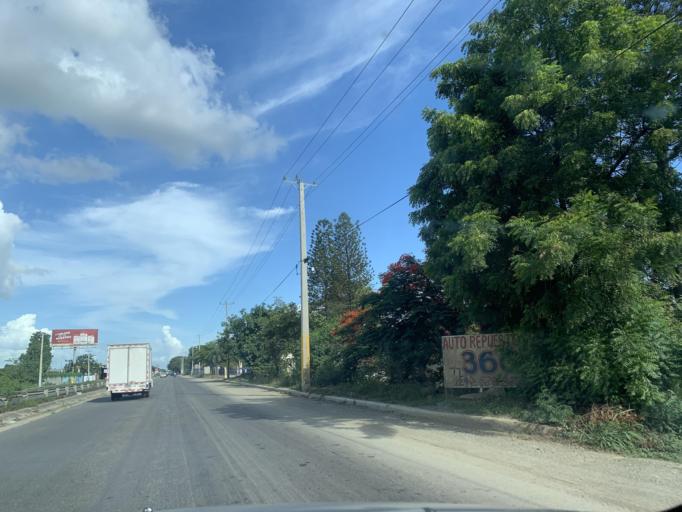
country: DO
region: Santiago
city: Villa Gonzalez
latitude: 19.5481
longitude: -70.8097
